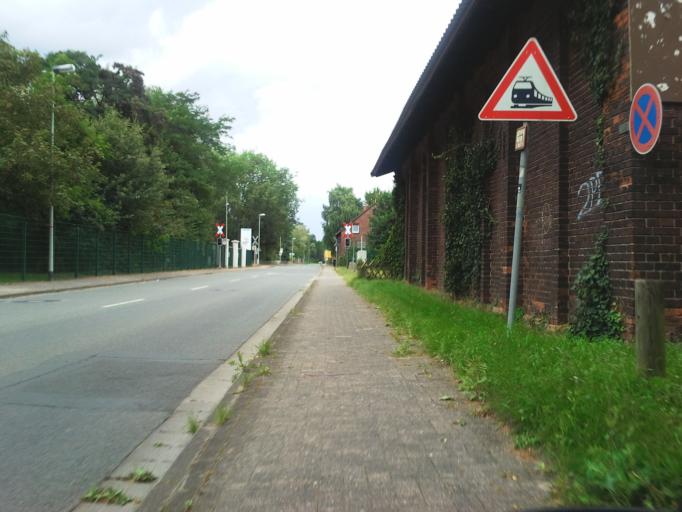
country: DE
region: Lower Saxony
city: Nienburg
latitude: 52.6538
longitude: 9.2098
